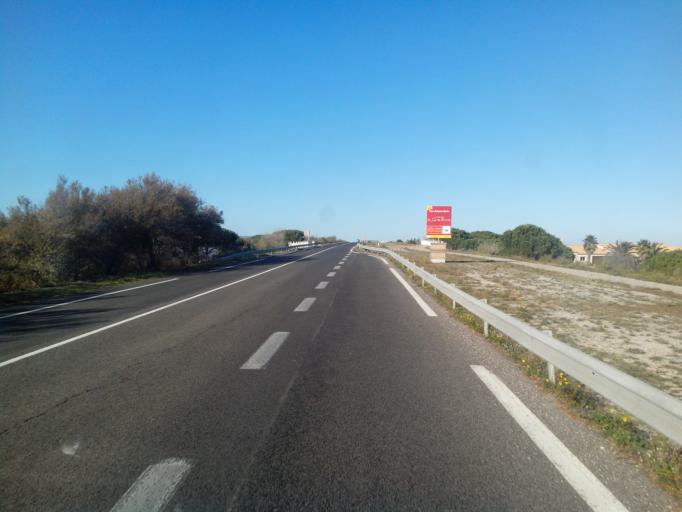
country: FR
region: Languedoc-Roussillon
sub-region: Departement de l'Aude
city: Leucate
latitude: 42.8520
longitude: 3.0353
